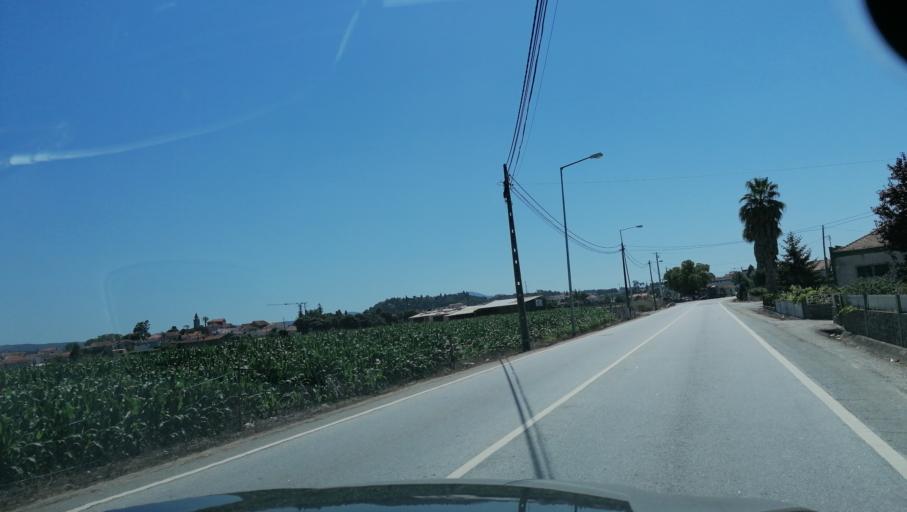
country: PT
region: Aveiro
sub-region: Anadia
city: Arcos
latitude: 40.4577
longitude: -8.4549
